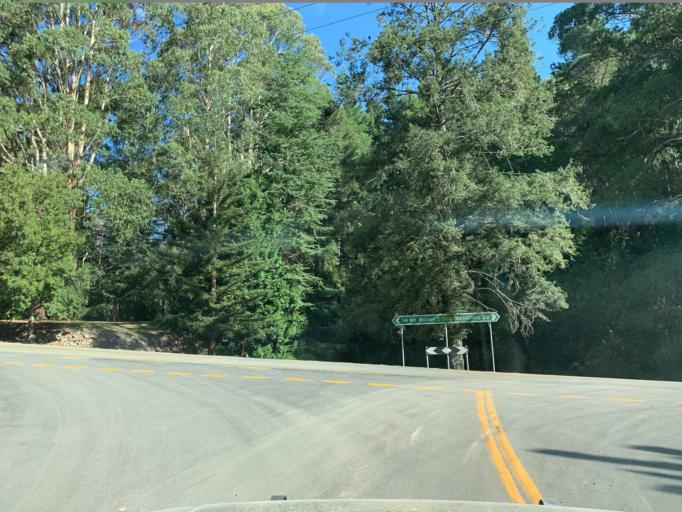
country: AU
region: Victoria
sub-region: Mansfield
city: Mansfield
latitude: -37.1104
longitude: 146.4000
